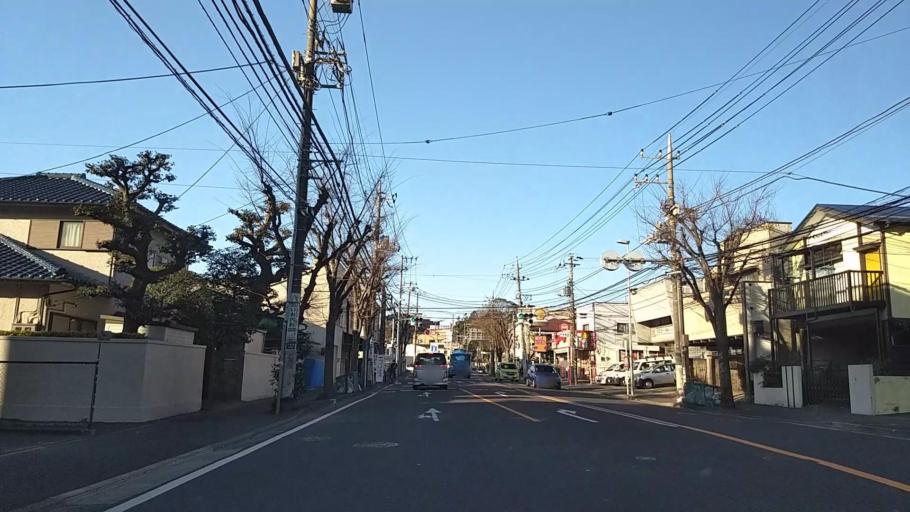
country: JP
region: Kanagawa
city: Fujisawa
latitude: 35.3936
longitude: 139.5292
